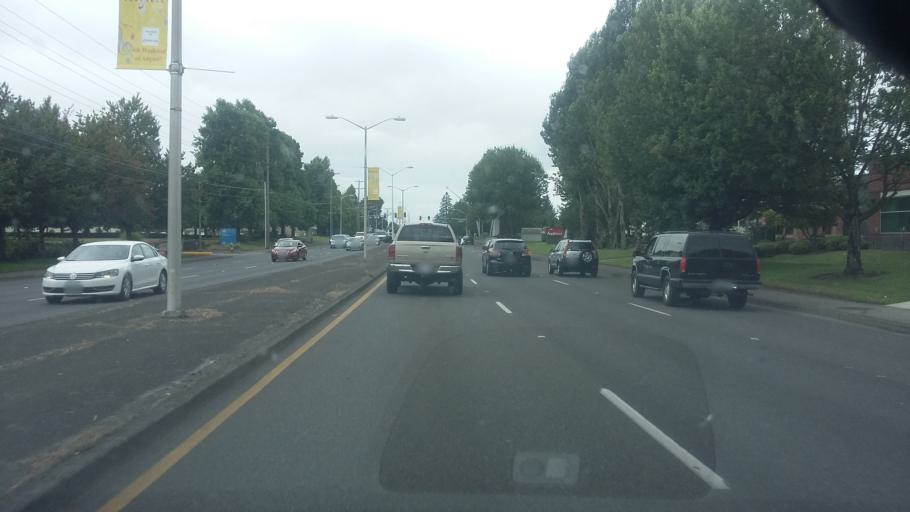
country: US
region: Washington
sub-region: Clark County
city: Mill Plain
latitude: 45.6194
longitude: -122.5397
